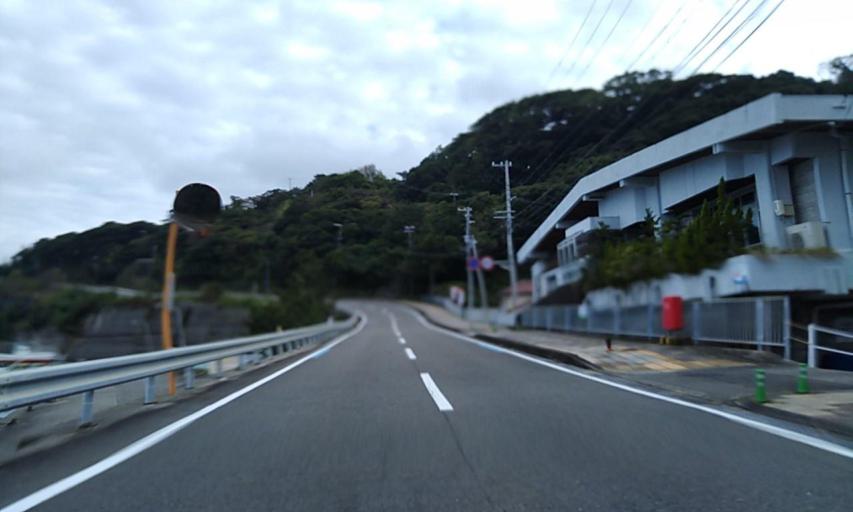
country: JP
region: Wakayama
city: Shingu
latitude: 33.5897
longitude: 135.9478
